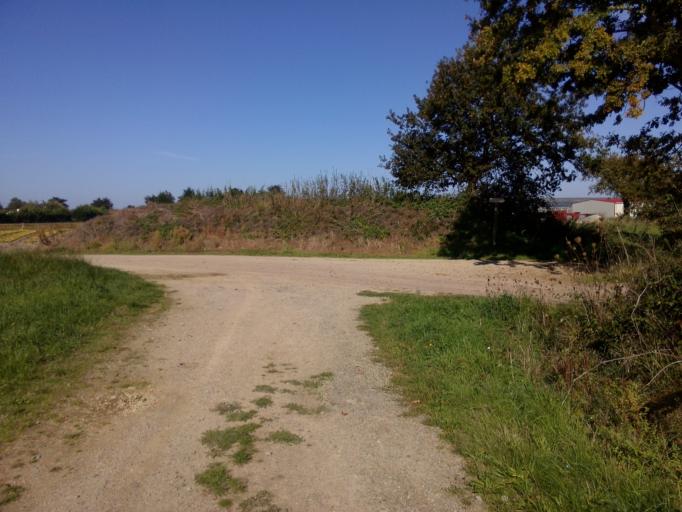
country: FR
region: Pays de la Loire
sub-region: Departement de la Loire-Atlantique
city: Arthon-en-Retz
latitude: 47.1136
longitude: -1.9316
